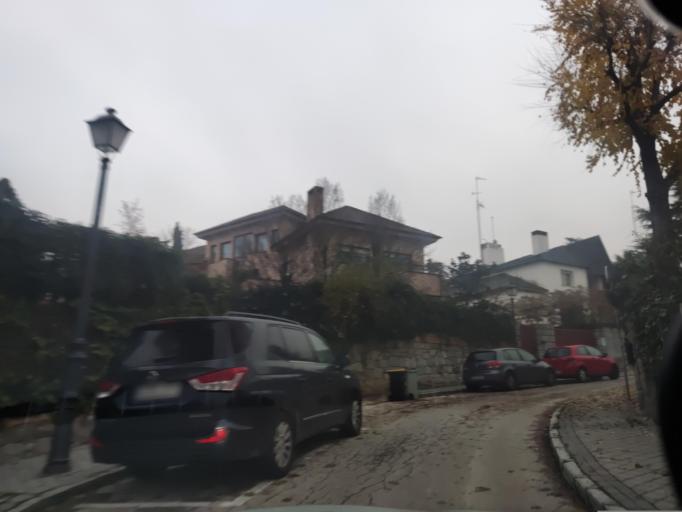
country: ES
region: Madrid
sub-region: Provincia de Madrid
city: Tetuan de las Victorias
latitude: 40.4902
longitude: -3.7045
